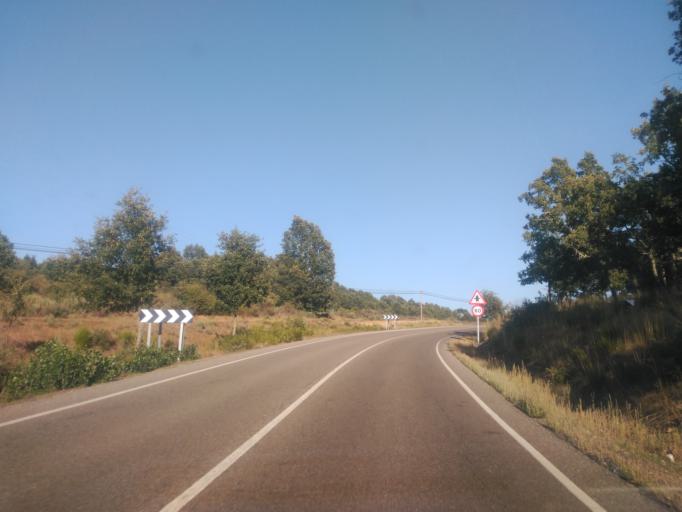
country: ES
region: Castille and Leon
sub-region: Provincia de Zamora
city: Puebla de Sanabria
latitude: 42.0806
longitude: -6.6261
